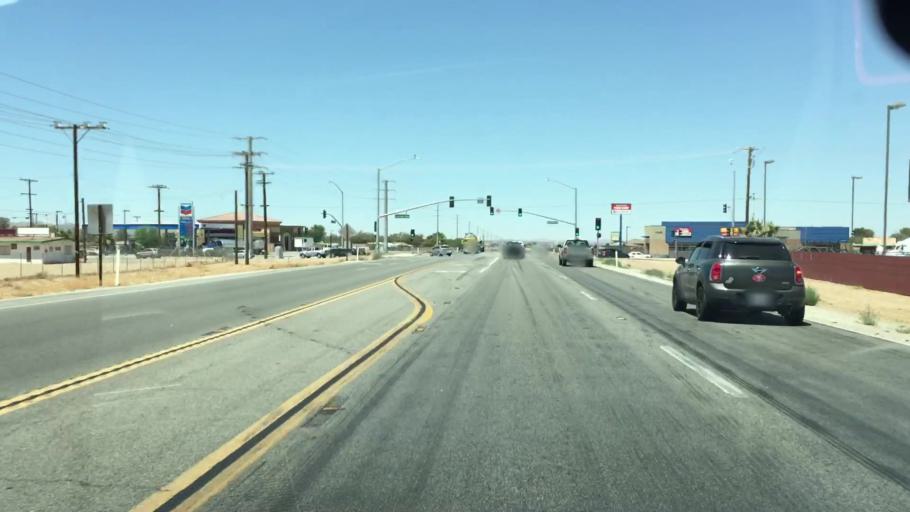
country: US
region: California
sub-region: San Bernardino County
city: Adelanto
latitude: 34.5782
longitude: -117.4117
